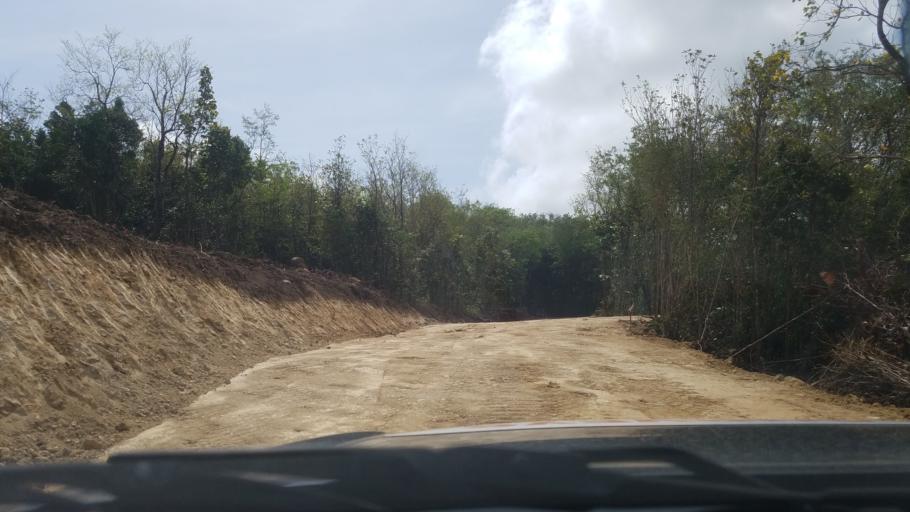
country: LC
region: Gros-Islet
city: Gros Islet
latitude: 14.0476
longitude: -60.9600
